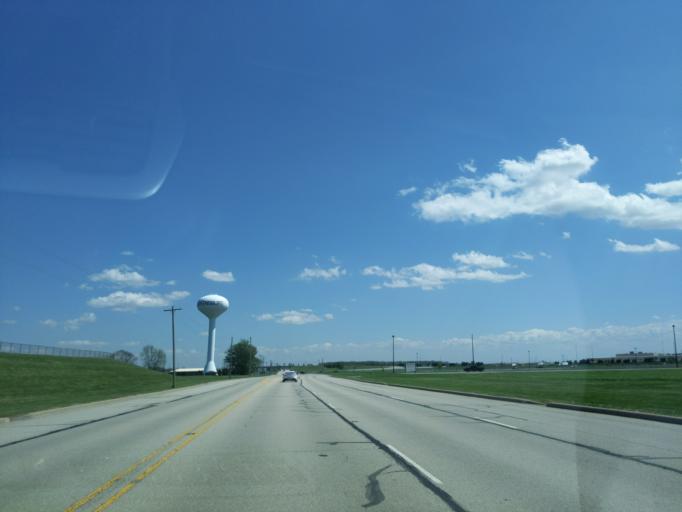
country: US
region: Indiana
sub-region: Decatur County
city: Greensburg
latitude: 39.3812
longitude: -85.5441
